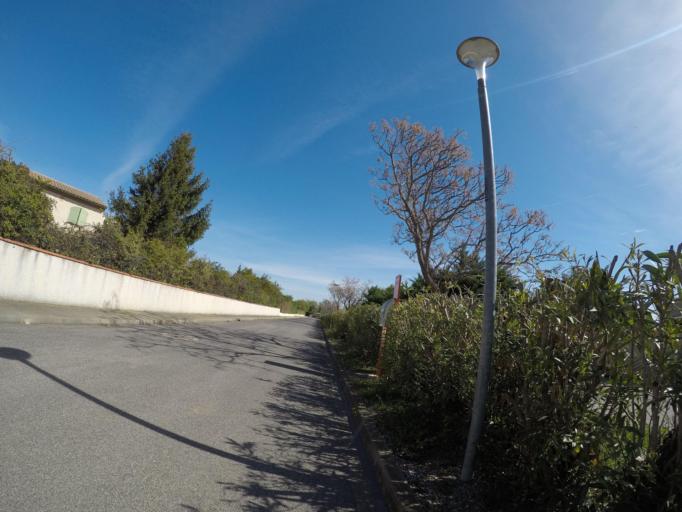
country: FR
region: Languedoc-Roussillon
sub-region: Departement des Pyrenees-Orientales
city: Millas
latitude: 42.6460
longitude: 2.7052
